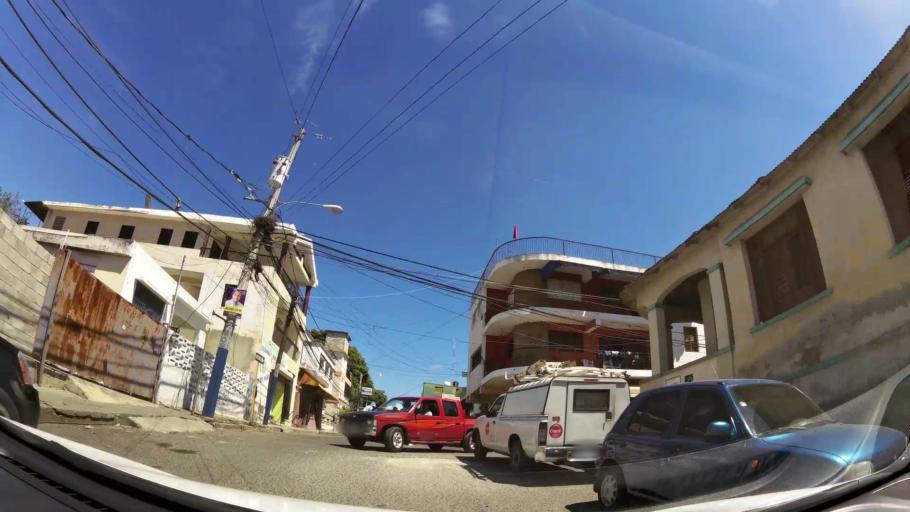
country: DO
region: Santiago
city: Santiago de los Caballeros
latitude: 19.4526
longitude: -70.7087
